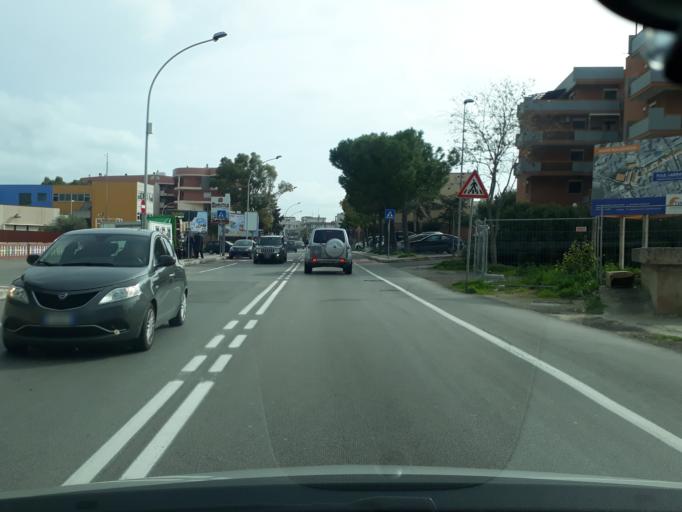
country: IT
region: Apulia
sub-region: Provincia di Bari
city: Monopoli
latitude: 40.9499
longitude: 17.2887
